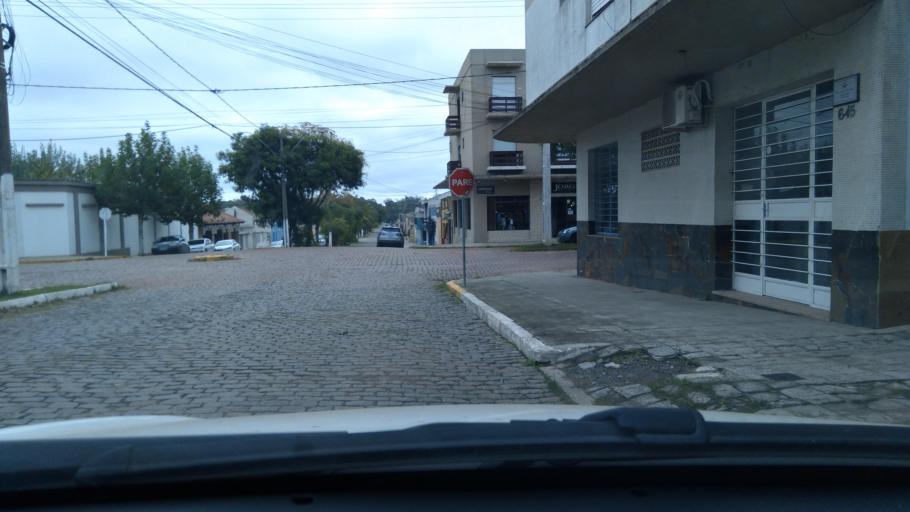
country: BR
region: Rio Grande do Sul
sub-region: Dom Pedrito
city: Dom Pedrito
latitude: -30.9840
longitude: -54.6777
